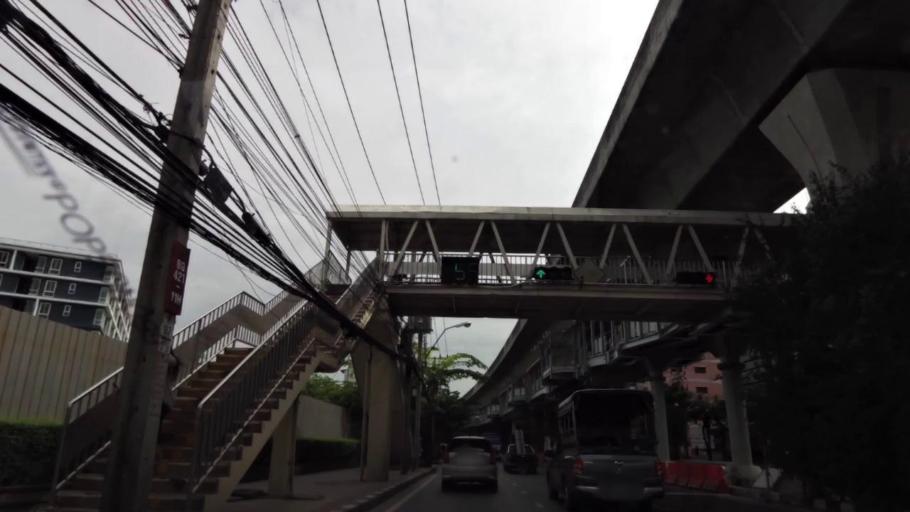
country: TH
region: Bangkok
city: Phra Khanong
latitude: 13.6844
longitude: 100.6104
